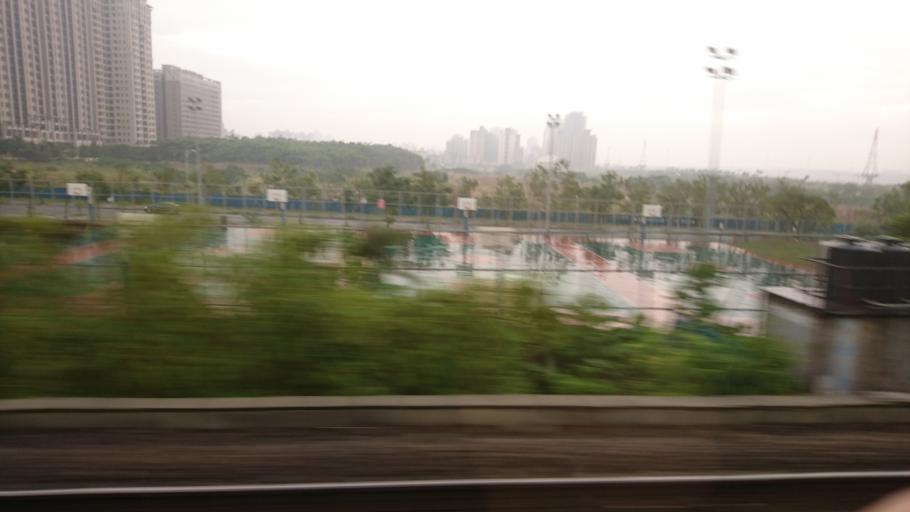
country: TW
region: Taiwan
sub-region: Hsinchu
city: Zhubei
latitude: 24.8257
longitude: 121.0000
